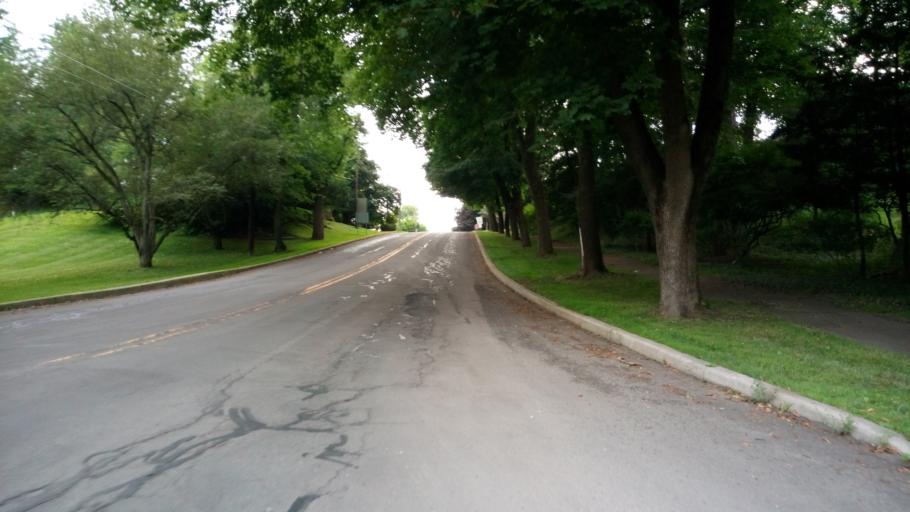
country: US
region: New York
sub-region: Chemung County
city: West Elmira
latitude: 42.0883
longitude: -76.8298
